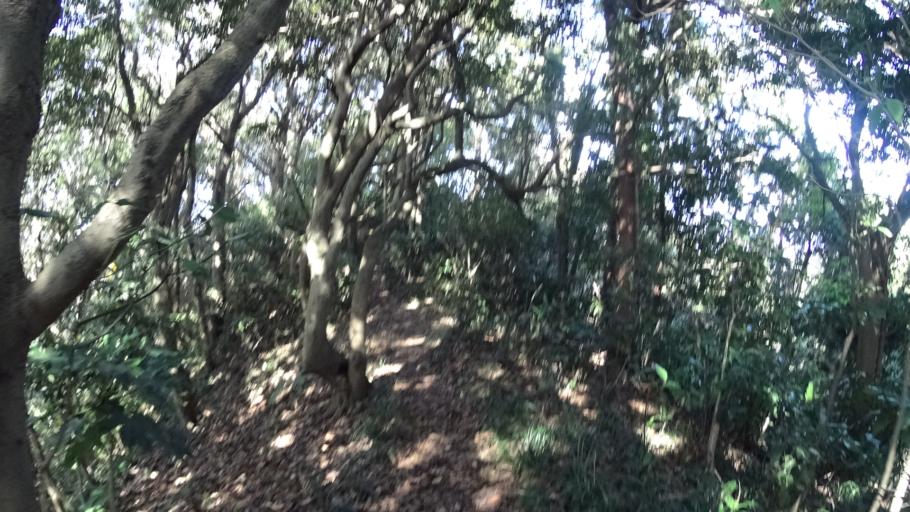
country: JP
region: Kanagawa
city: Hayama
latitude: 35.2769
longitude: 139.6088
